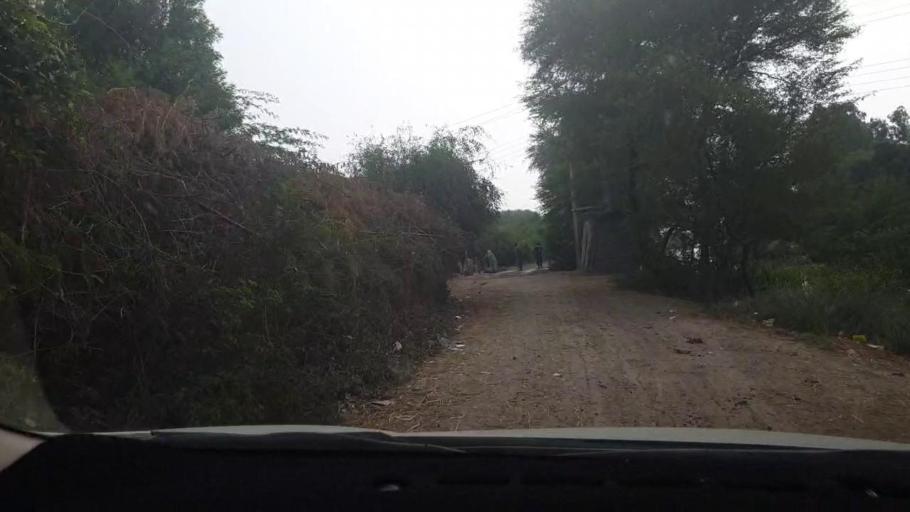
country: PK
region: Sindh
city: Tando Muhammad Khan
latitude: 25.0595
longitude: 68.5082
